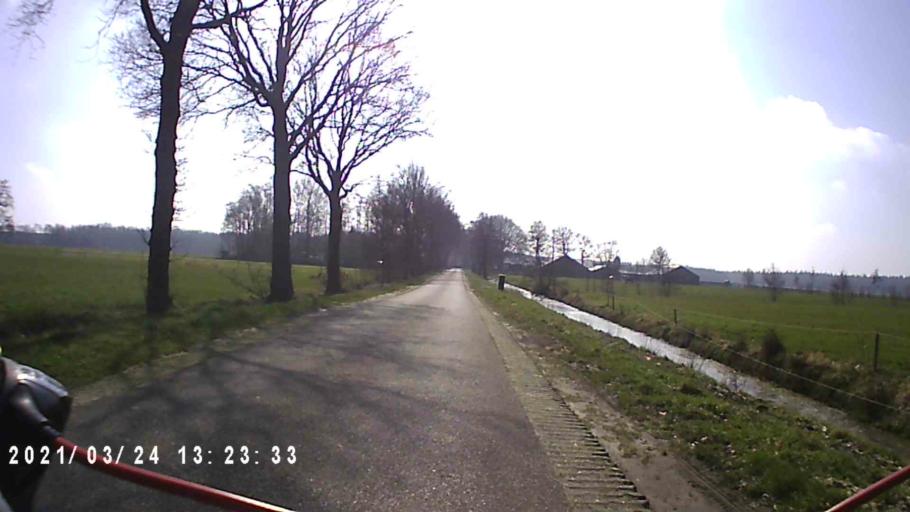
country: NL
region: Groningen
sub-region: Gemeente Grootegast
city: Grootegast
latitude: 53.0988
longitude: 6.2763
